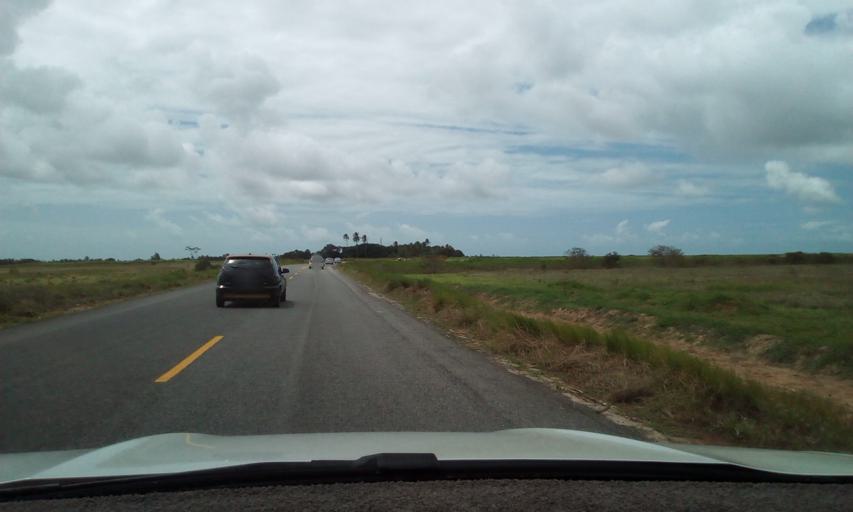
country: BR
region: Paraiba
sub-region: Rio Tinto
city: Rio Tinto
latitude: -6.7720
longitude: -35.0354
